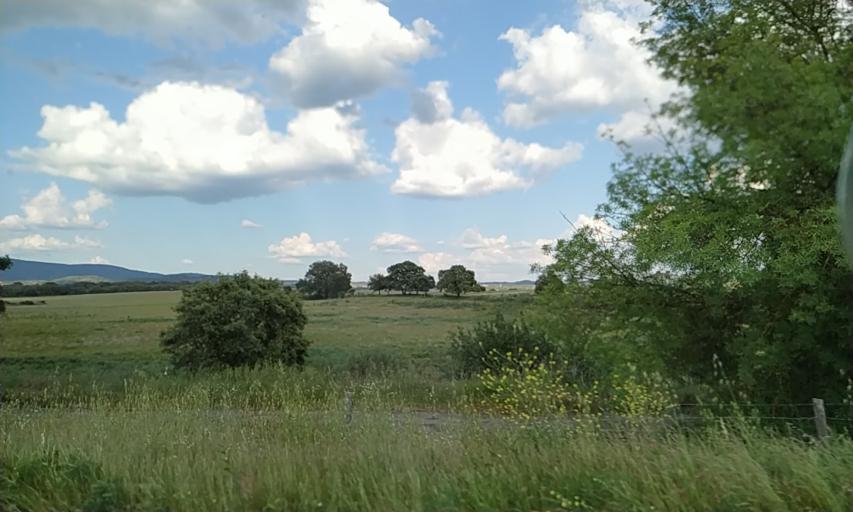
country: PT
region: Portalegre
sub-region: Portalegre
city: Urra
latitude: 39.2424
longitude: -7.4507
